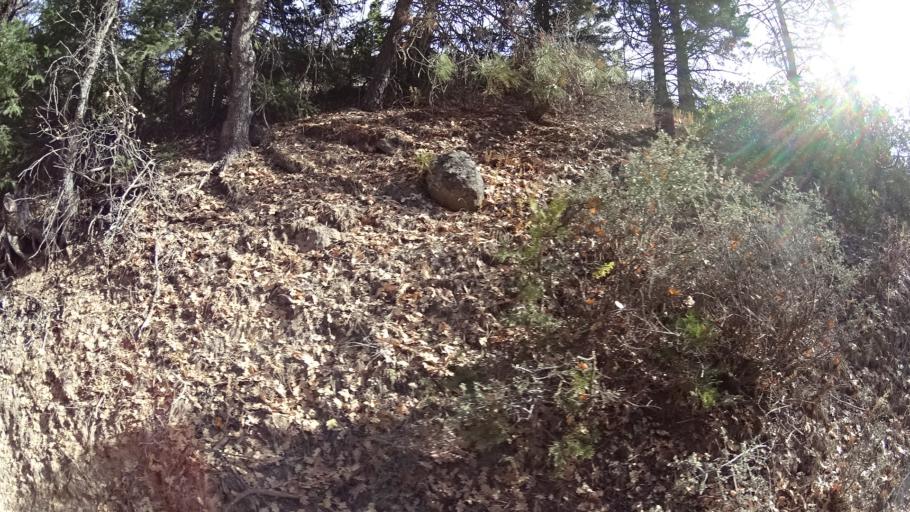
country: US
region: California
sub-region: Siskiyou County
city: Weed
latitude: 41.4403
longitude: -122.4248
